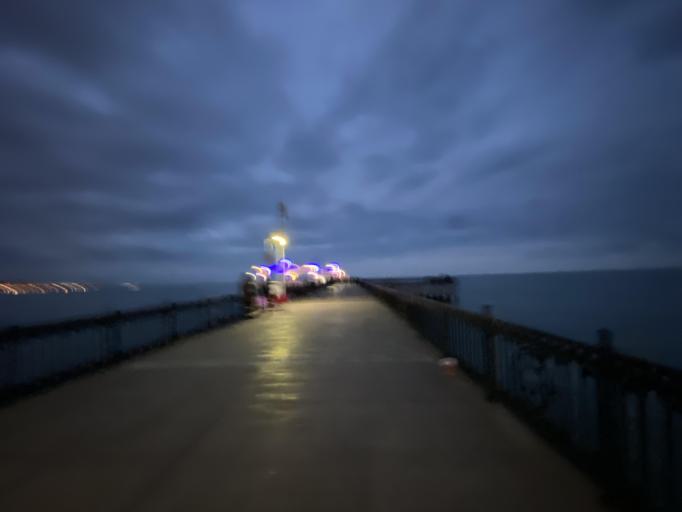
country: TR
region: Samsun
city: Samsun
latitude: 41.3453
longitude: 36.2619
